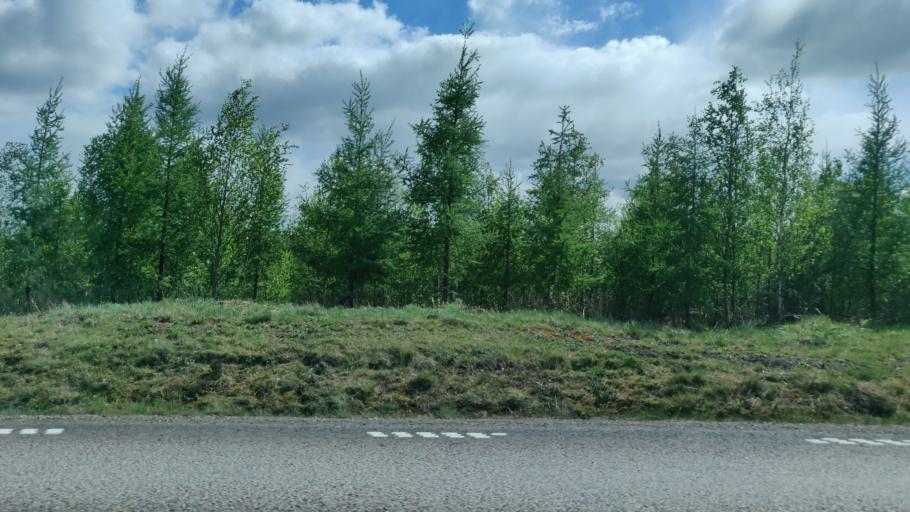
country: SE
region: Vaermland
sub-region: Karlstads Kommun
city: Molkom
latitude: 59.5539
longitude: 13.6612
